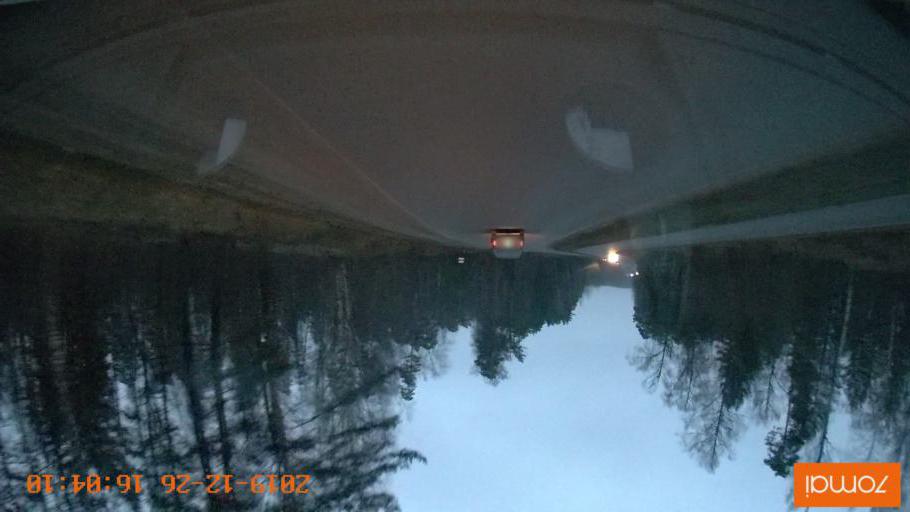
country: RU
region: Jaroslavl
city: Rybinsk
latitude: 58.0087
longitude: 38.8634
